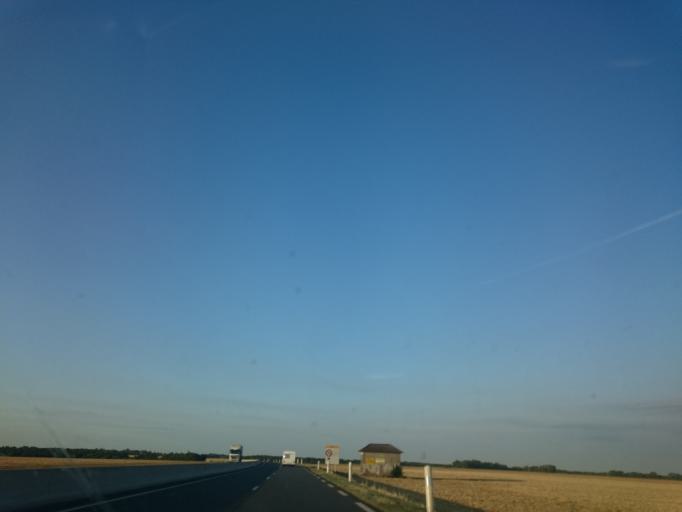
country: FR
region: Ile-de-France
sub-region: Departement de l'Essonne
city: Mereville
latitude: 48.3568
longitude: 2.0582
